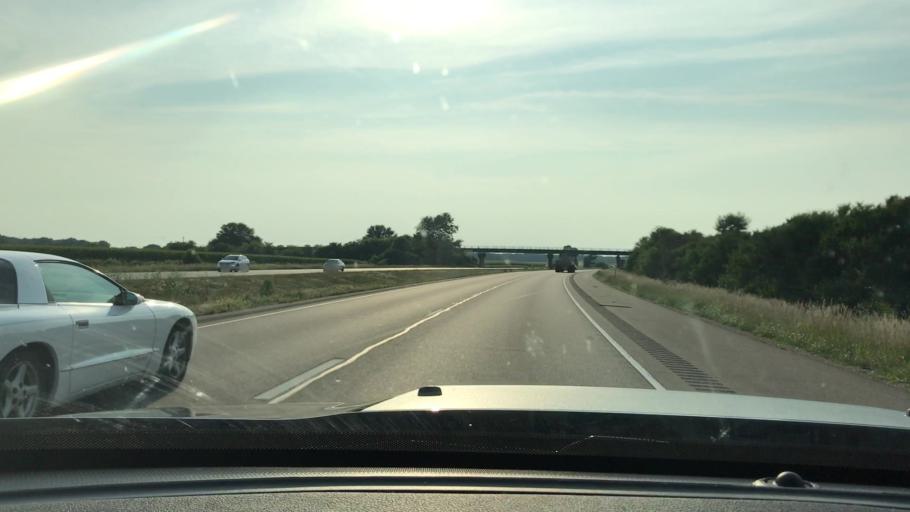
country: US
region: Illinois
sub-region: Bureau County
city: Princeton
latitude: 41.3874
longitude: -89.5458
